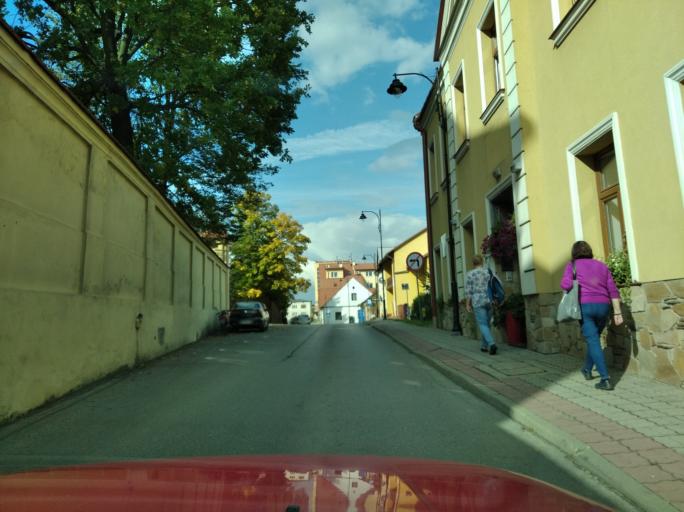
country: PL
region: Subcarpathian Voivodeship
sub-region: Powiat rzeszowski
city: Tyczyn
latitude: 49.9620
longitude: 22.0343
